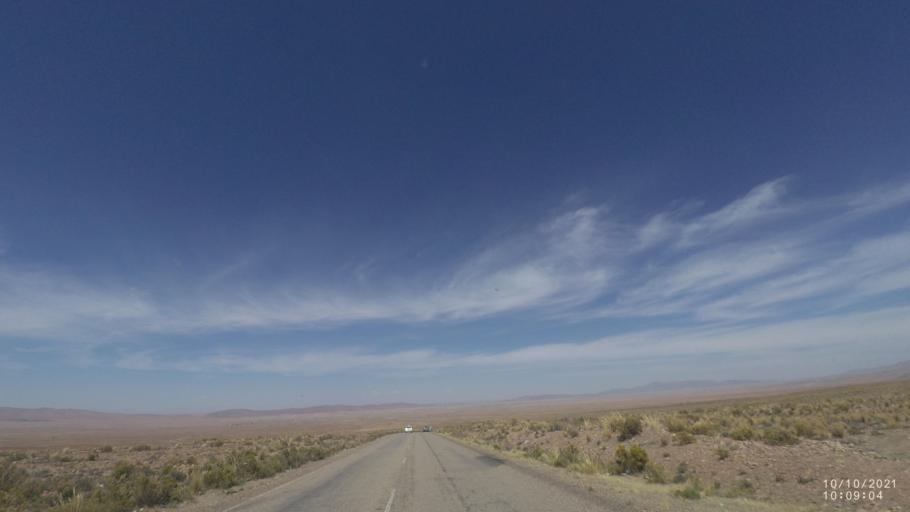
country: BO
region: La Paz
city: Eucaliptus
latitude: -17.3971
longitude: -67.4840
